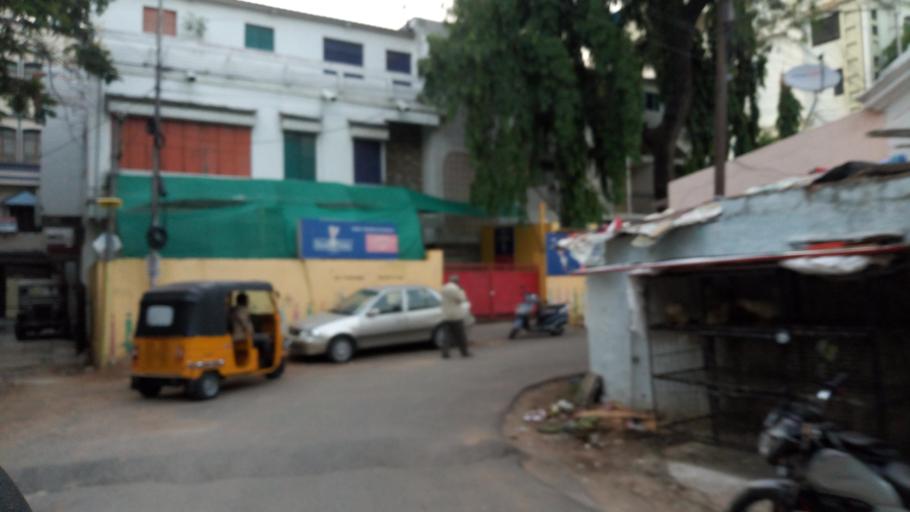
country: IN
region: Telangana
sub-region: Hyderabad
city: Hyderabad
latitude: 17.4019
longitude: 78.4726
